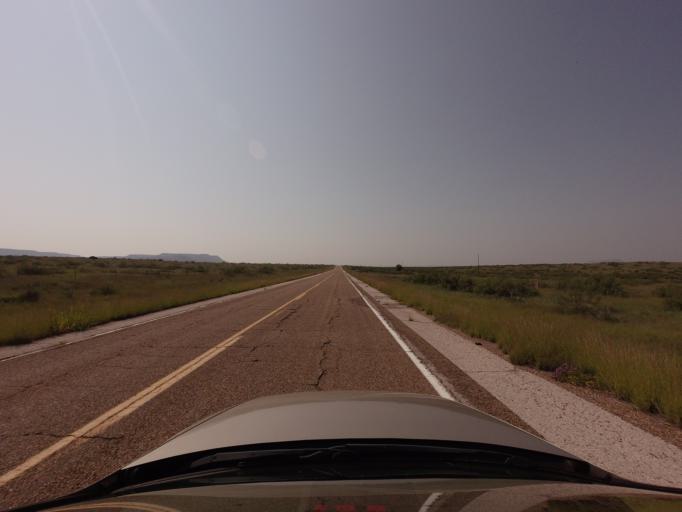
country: US
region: New Mexico
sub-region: Quay County
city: Tucumcari
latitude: 35.0306
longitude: -103.7375
